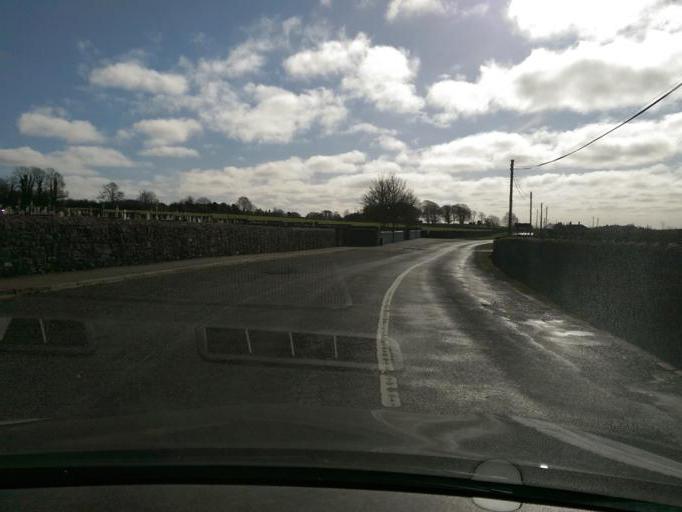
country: IE
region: Connaught
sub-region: County Galway
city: Ballinasloe
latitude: 53.3952
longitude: -8.3293
